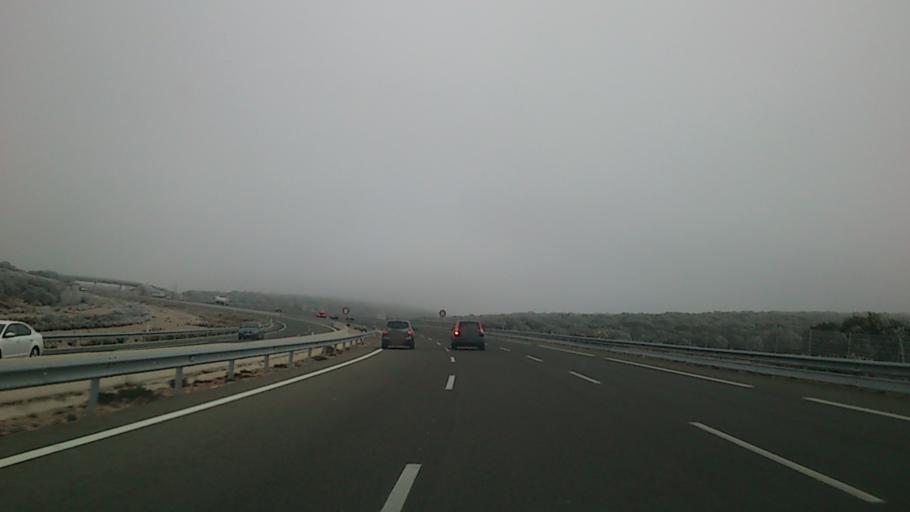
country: ES
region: Castille-La Mancha
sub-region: Provincia de Guadalajara
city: Sauca
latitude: 41.0191
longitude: -2.5216
